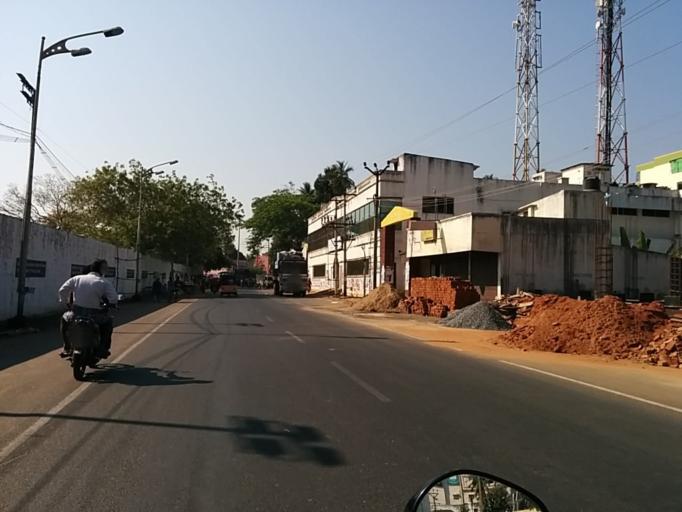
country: IN
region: Pondicherry
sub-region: Puducherry
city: Puducherry
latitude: 11.9551
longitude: 79.8277
